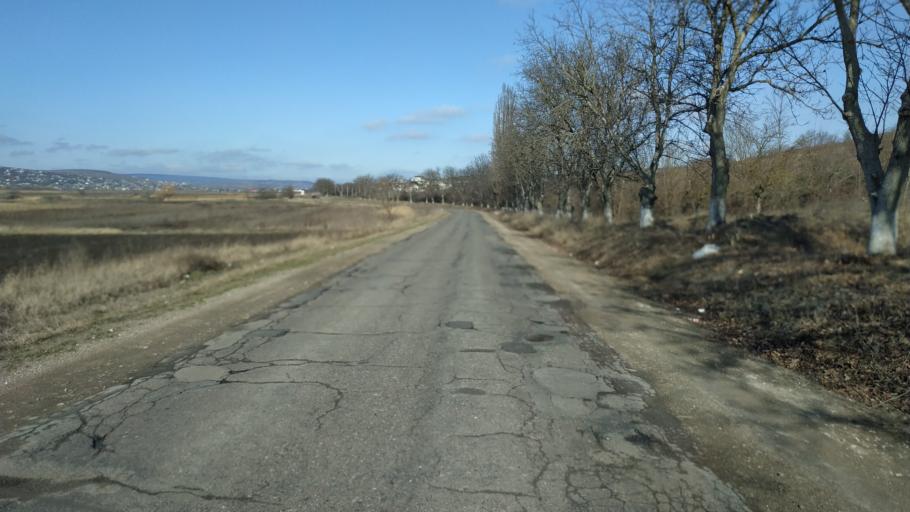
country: MD
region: Laloveni
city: Ialoveni
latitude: 46.9235
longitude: 28.6842
